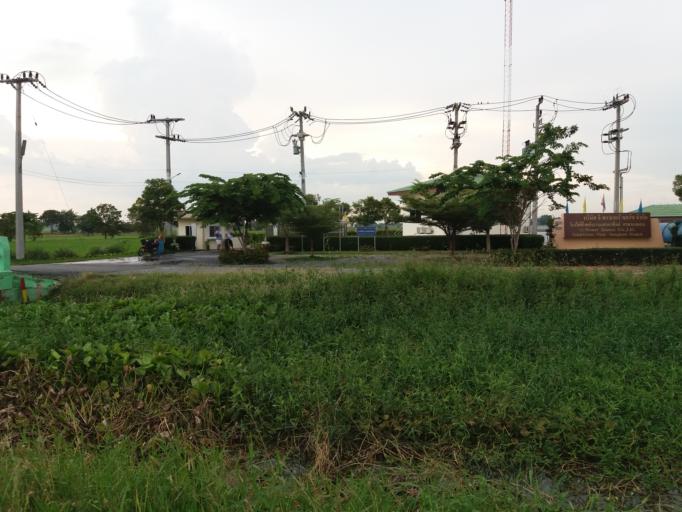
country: TH
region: Suphan Buri
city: Doem Bang Nang Buat
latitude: 14.9263
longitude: 100.1443
